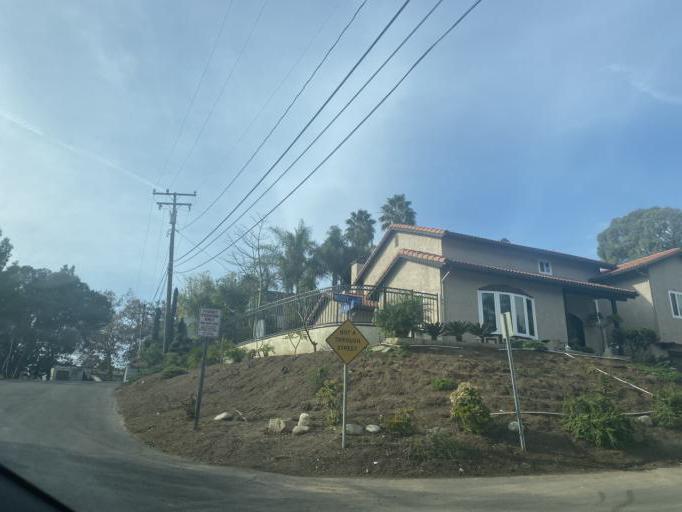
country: US
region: California
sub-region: Orange County
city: Placentia
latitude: 33.8909
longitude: -117.8890
